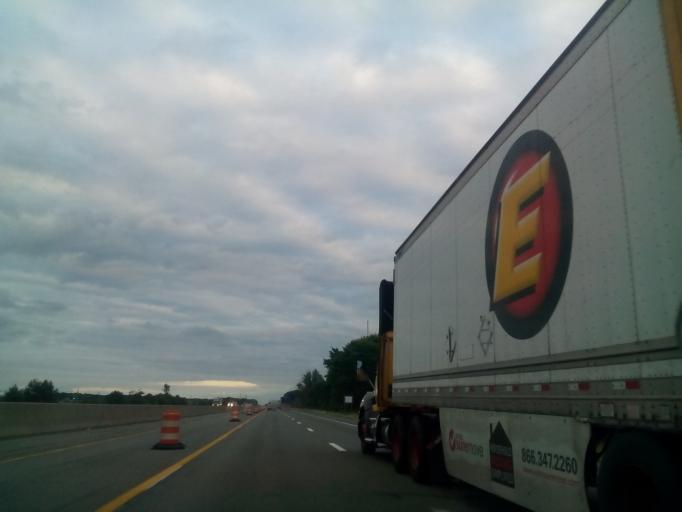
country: US
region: Ohio
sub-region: Trumbull County
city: Lordstown
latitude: 41.1463
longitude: -80.8855
